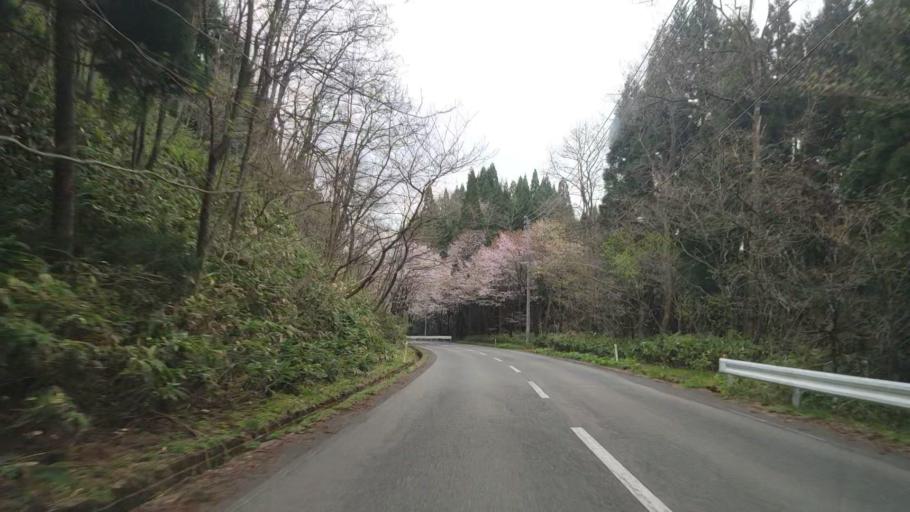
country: JP
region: Akita
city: Hanawa
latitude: 40.3667
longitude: 140.7853
